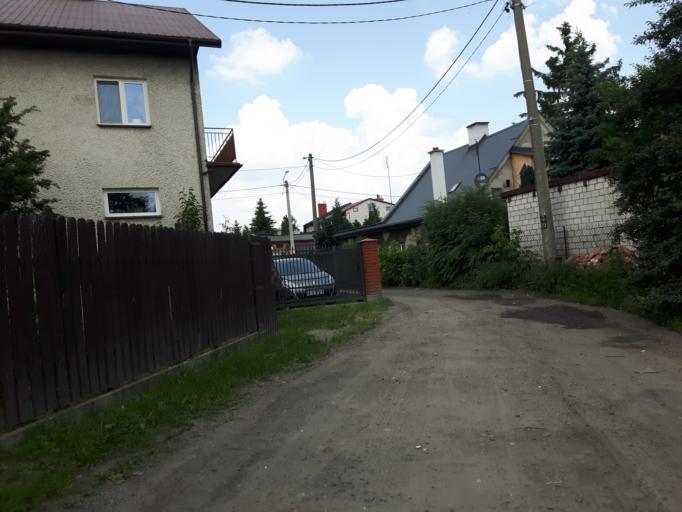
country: PL
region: Masovian Voivodeship
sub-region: Powiat wolominski
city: Zabki
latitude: 52.2835
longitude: 21.1166
